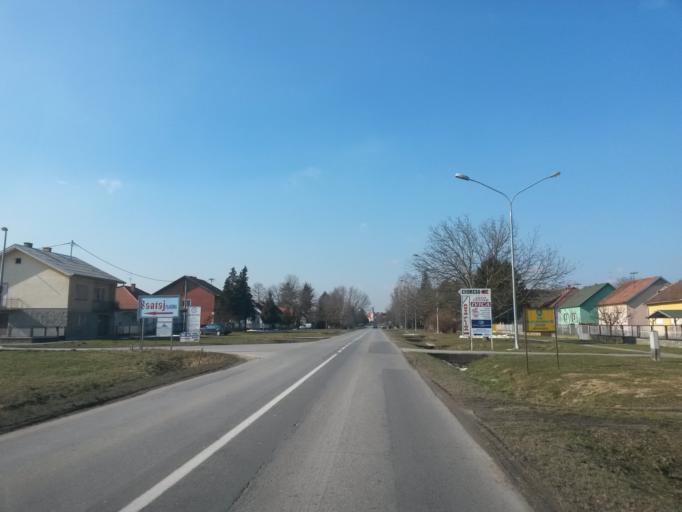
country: HR
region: Osjecko-Baranjska
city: Valpovo
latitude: 45.6537
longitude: 18.4292
